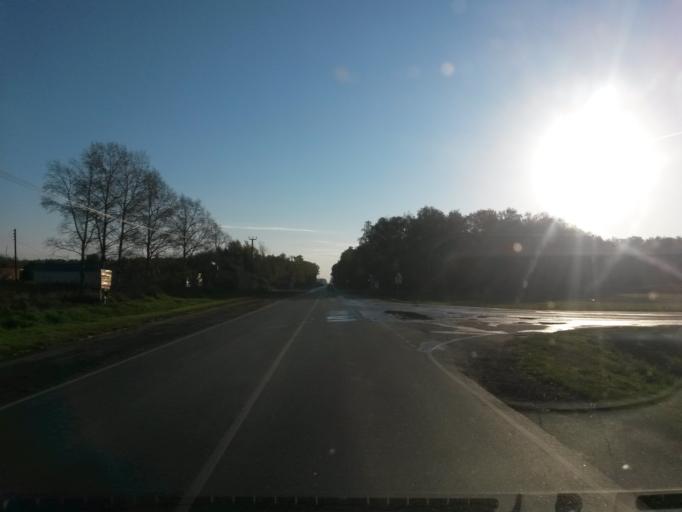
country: RU
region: Moskovskaya
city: Melikhovo
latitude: 55.1917
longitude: 37.7537
